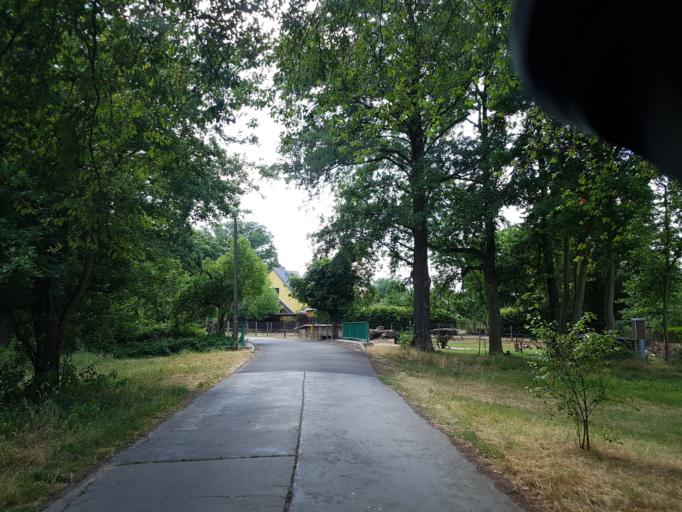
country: DE
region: Brandenburg
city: Cottbus
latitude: 51.7211
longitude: 14.3510
